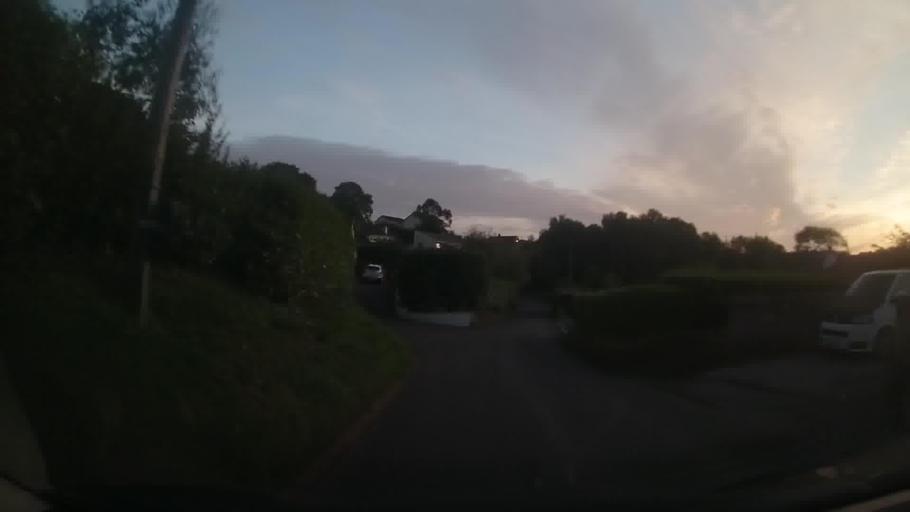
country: GB
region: Wales
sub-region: Pembrokeshire
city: Saundersfoot
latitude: 51.7286
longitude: -4.6787
